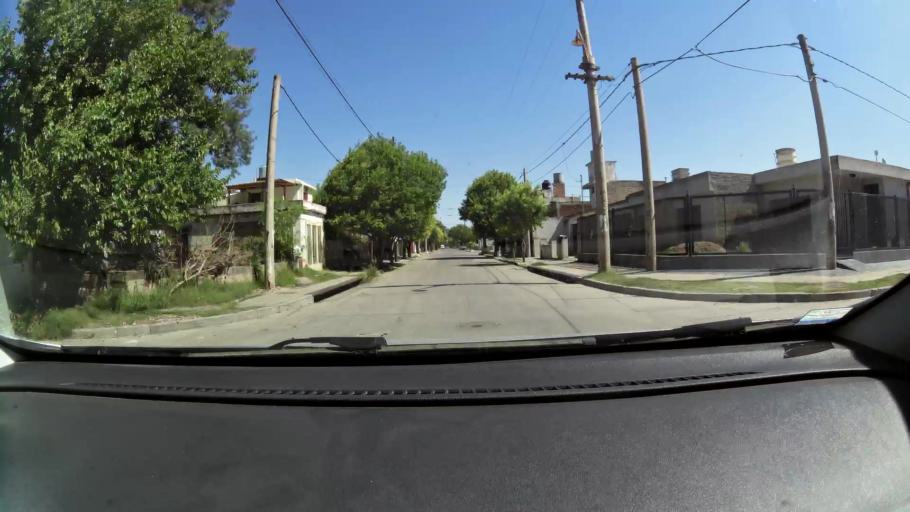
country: AR
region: Cordoba
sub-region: Departamento de Capital
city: Cordoba
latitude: -31.3690
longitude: -64.1365
